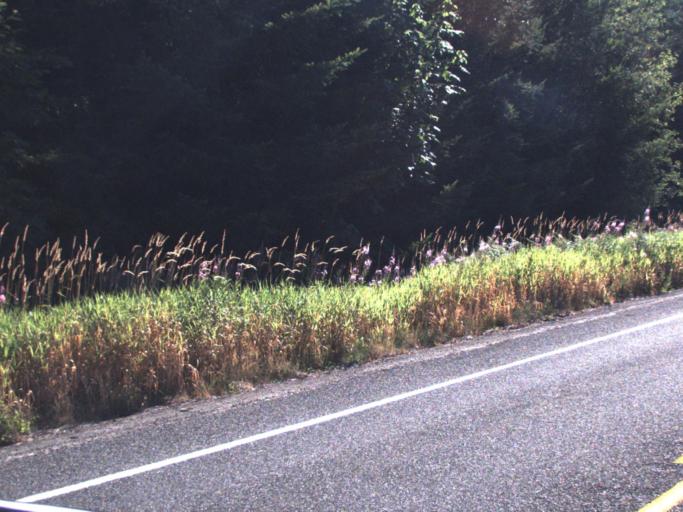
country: US
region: Washington
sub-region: King County
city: Enumclaw
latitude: 47.1552
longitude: -121.8590
